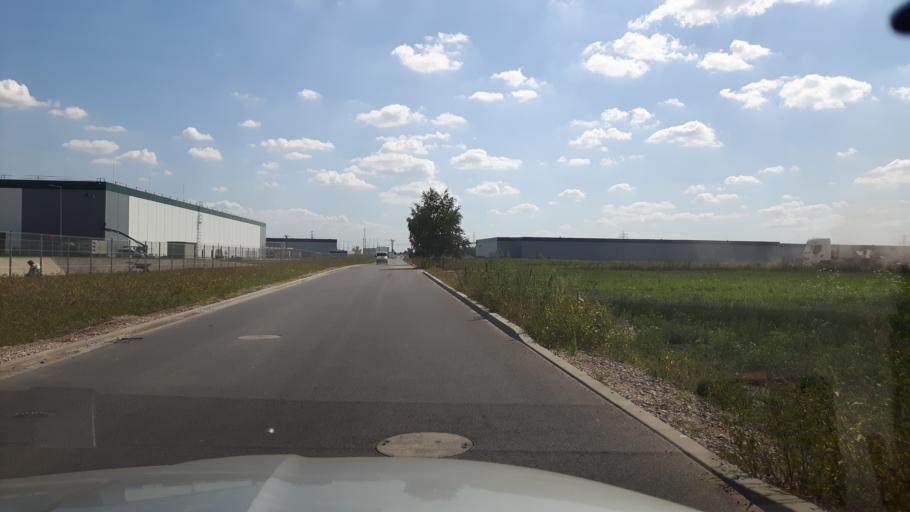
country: PL
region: Masovian Voivodeship
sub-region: Powiat pruszkowski
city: Michalowice
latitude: 52.1321
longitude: 20.8628
